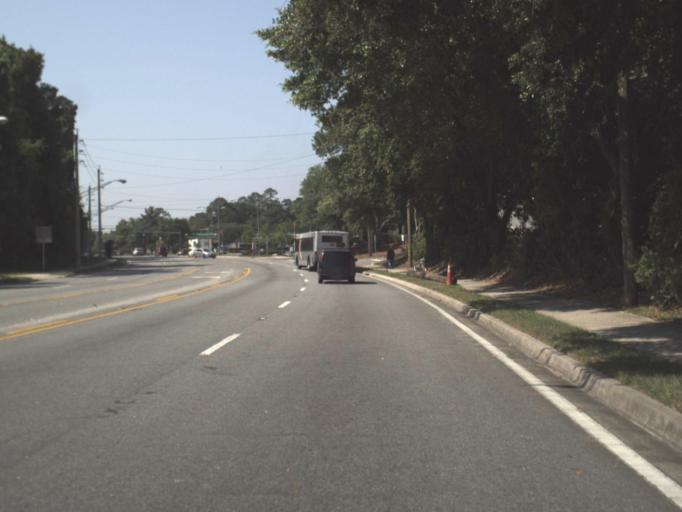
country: US
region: Florida
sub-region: Clay County
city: Bellair-Meadowbrook Terrace
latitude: 30.2724
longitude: -81.7560
